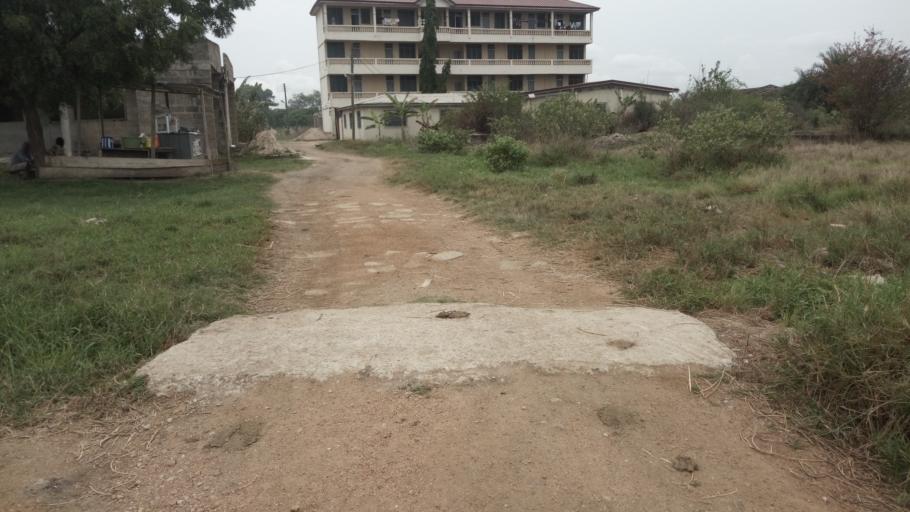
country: GH
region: Central
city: Winneba
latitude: 5.3622
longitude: -0.6395
